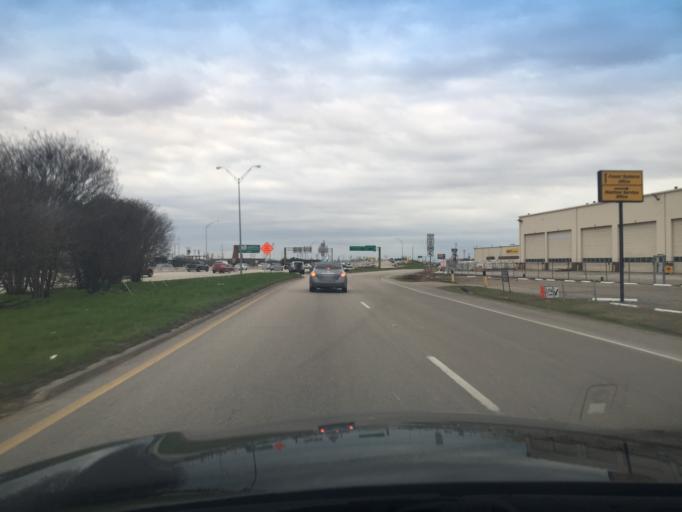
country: US
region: Texas
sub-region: Dallas County
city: Irving
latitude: 32.8353
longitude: -96.9157
